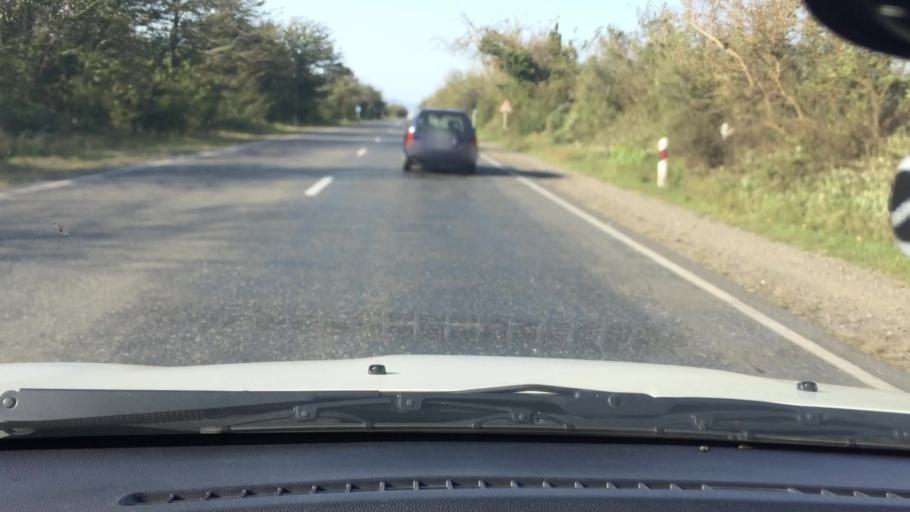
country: GE
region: Imereti
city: Vani
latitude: 42.2056
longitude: 42.5422
